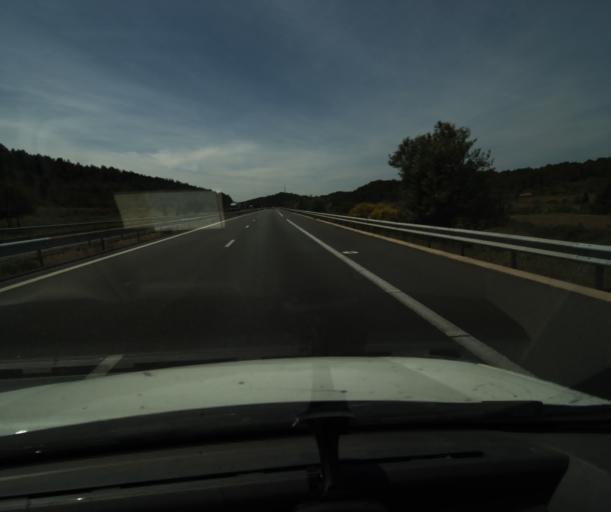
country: FR
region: Languedoc-Roussillon
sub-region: Departement de l'Aude
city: Puicheric
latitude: 43.1739
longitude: 2.6517
